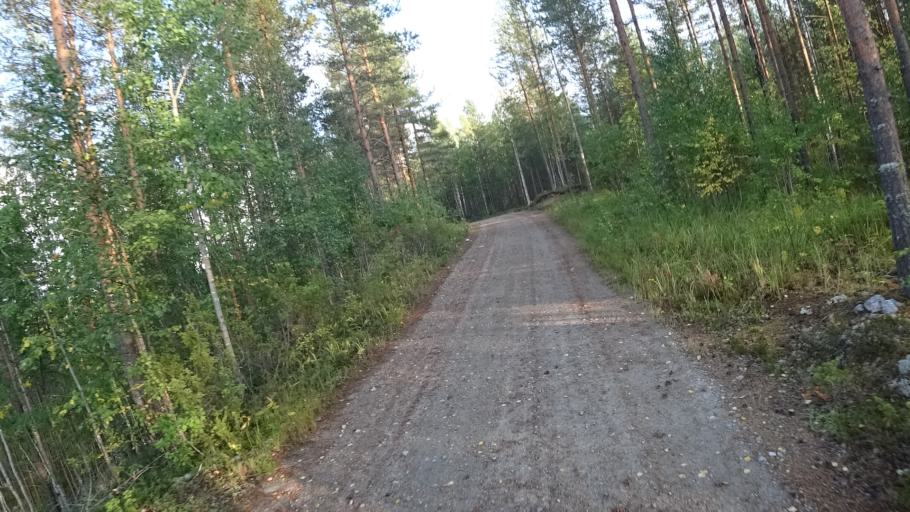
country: FI
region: North Karelia
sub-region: Joensuu
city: Ilomantsi
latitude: 62.6380
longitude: 31.0776
